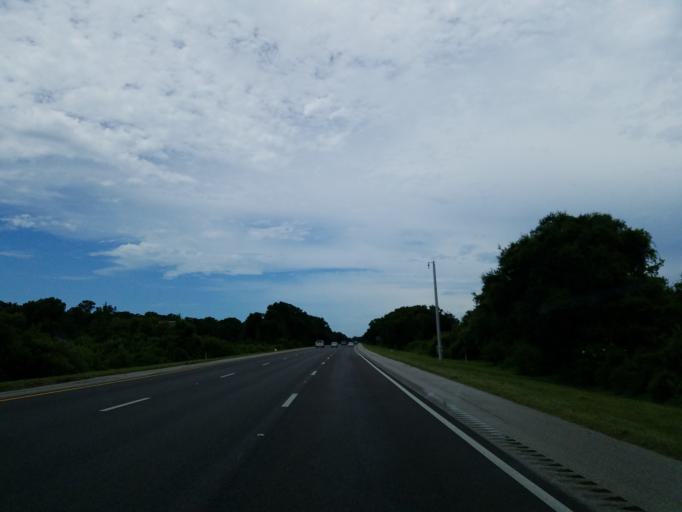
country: US
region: Florida
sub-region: Sarasota County
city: Lake Sarasota
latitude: 27.2483
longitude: -82.4502
